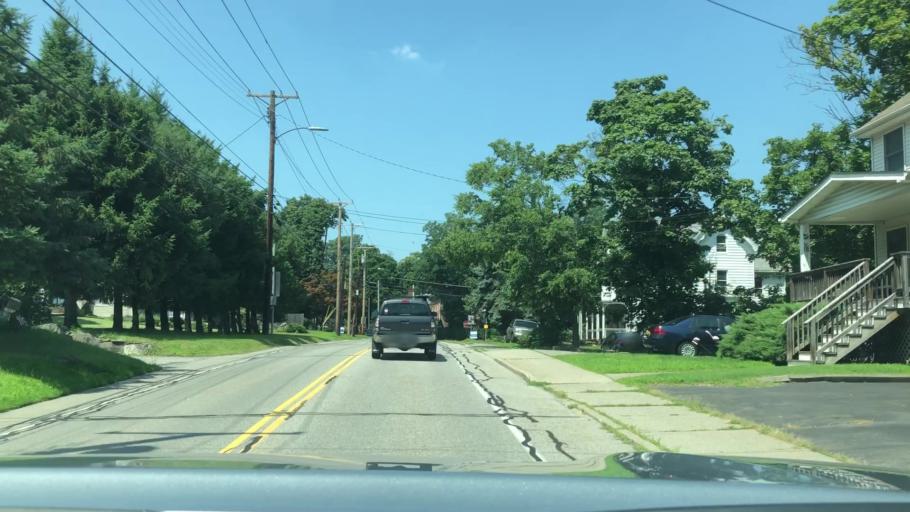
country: US
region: New York
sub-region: Dutchess County
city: Beacon
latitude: 41.4990
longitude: -73.9695
